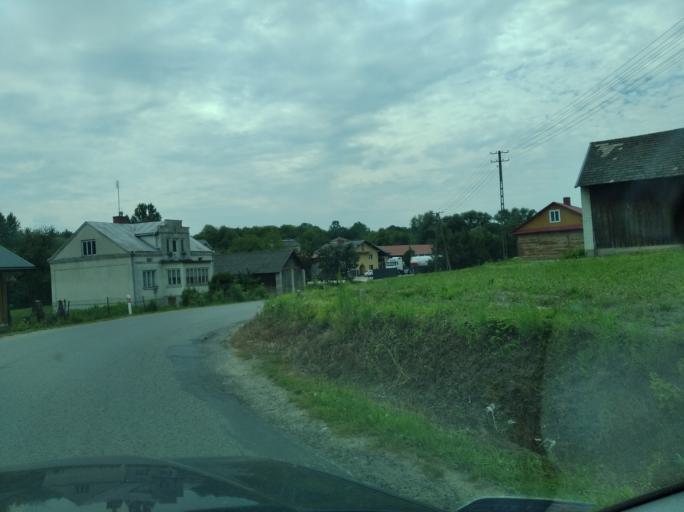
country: PL
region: Subcarpathian Voivodeship
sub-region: Powiat przeworski
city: Pantalowice
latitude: 49.9283
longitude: 22.4426
